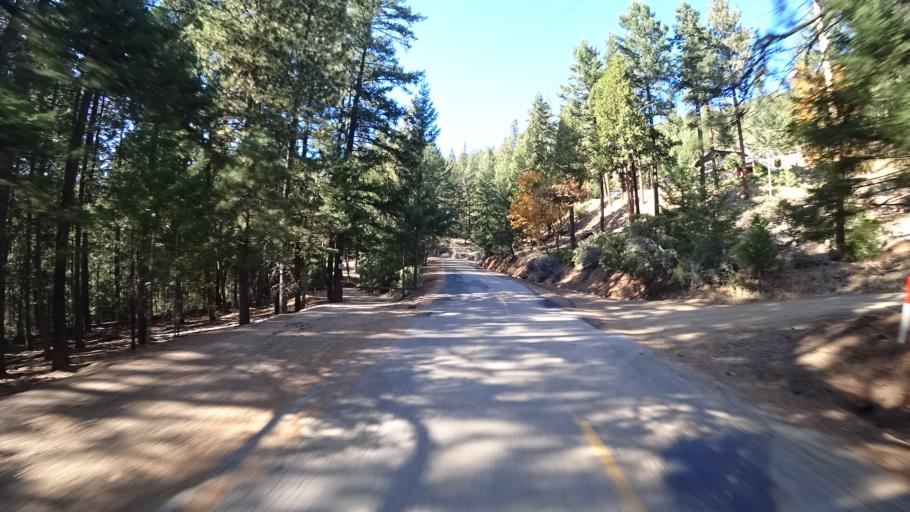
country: US
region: California
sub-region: Siskiyou County
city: Yreka
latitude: 41.7295
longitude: -122.7182
